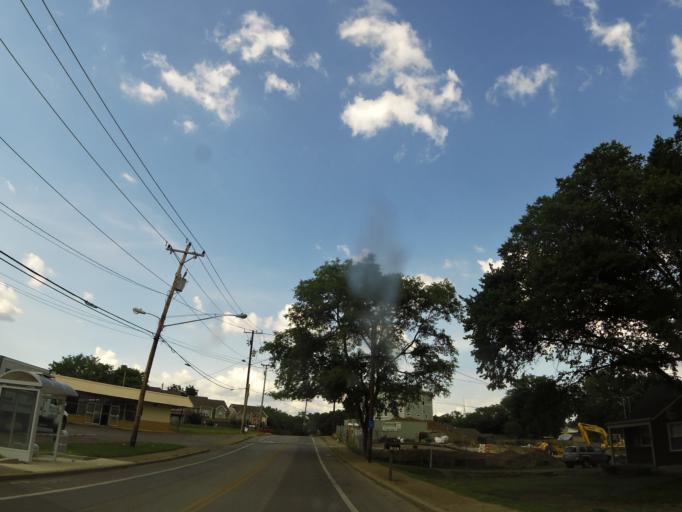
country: US
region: Tennessee
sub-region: Davidson County
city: Nashville
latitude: 36.1942
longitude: -86.7257
